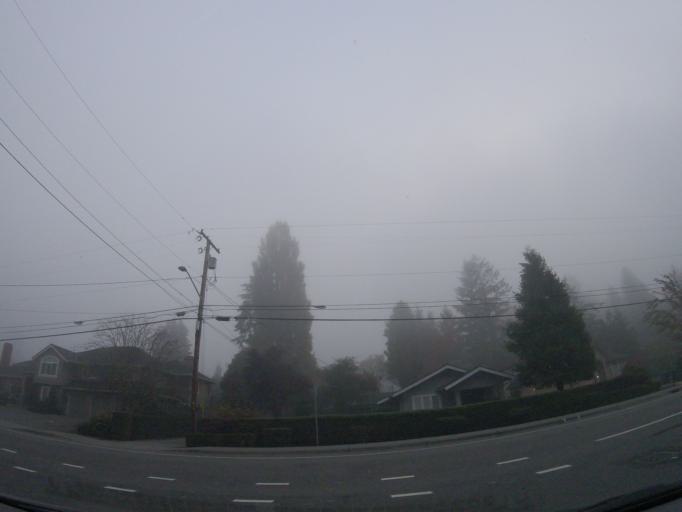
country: US
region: Washington
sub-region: King County
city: Bellevue
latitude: 47.6251
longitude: -122.1965
